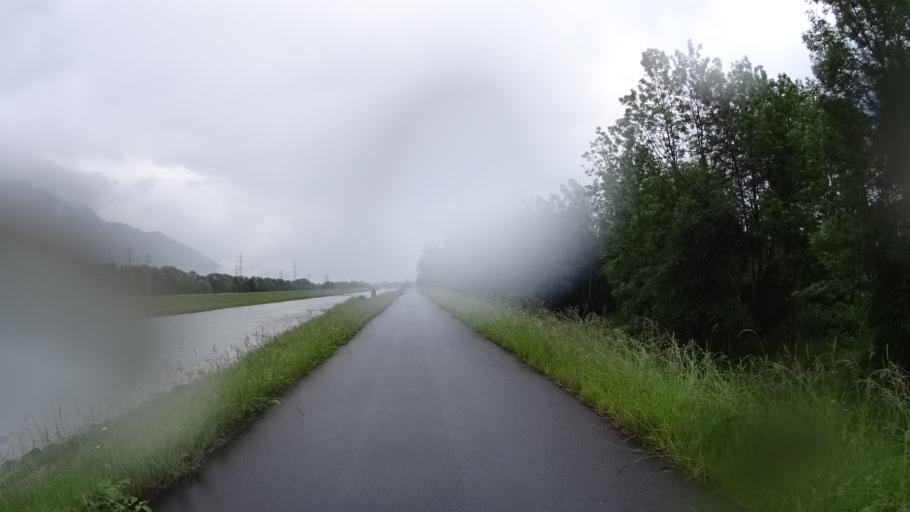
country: LI
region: Gamprin
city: Gamprin
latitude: 47.2269
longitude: 9.5073
